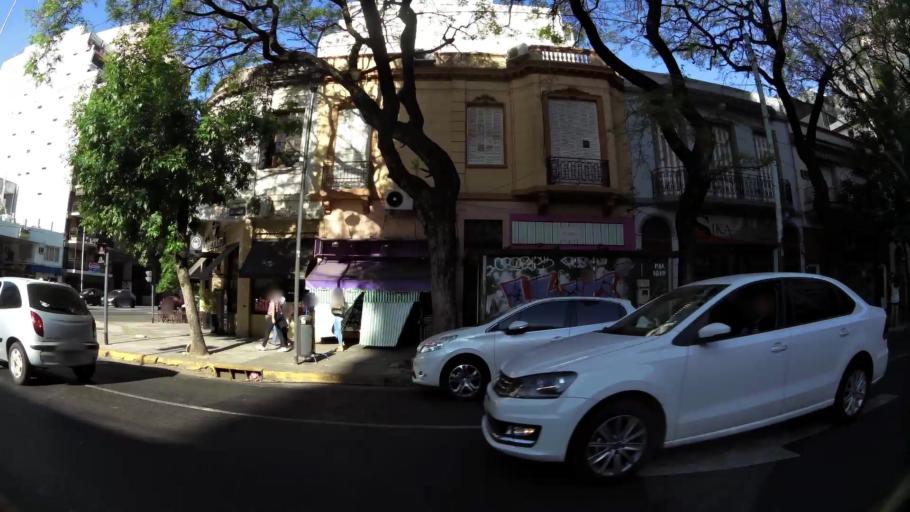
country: AR
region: Buenos Aires F.D.
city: Villa Santa Rita
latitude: -34.6233
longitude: -58.4346
